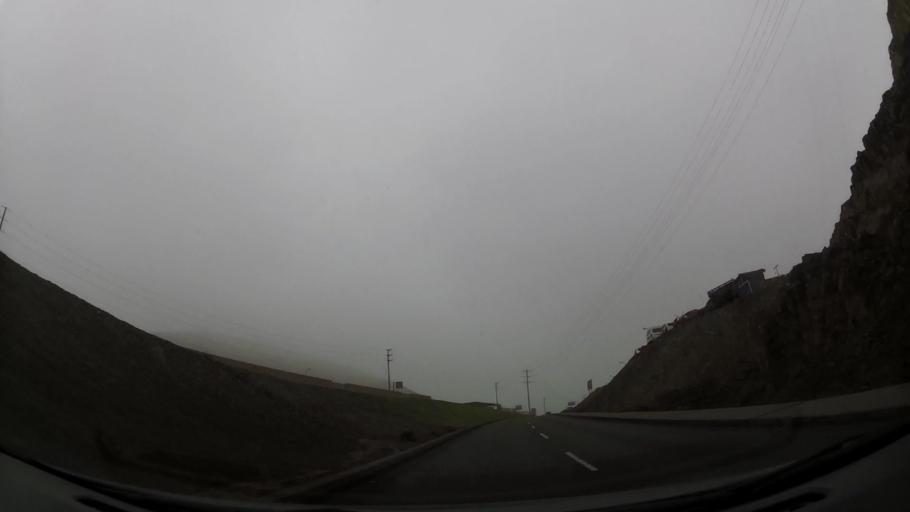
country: PE
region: Lima
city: Ventanilla
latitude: -11.8458
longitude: -77.1186
